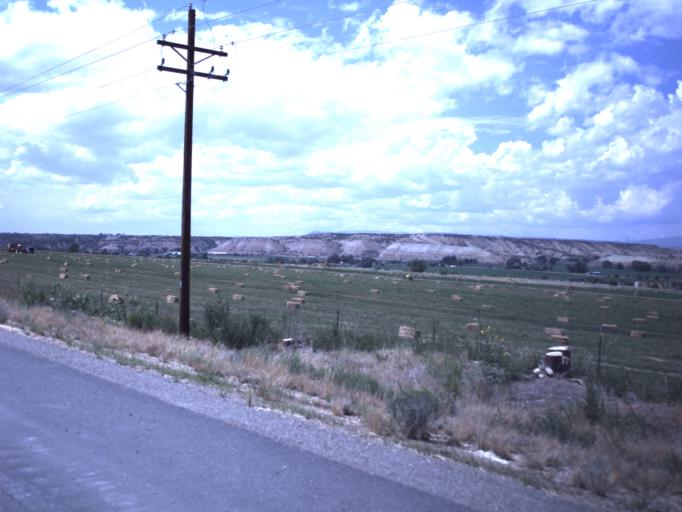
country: US
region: Utah
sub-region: Duchesne County
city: Duchesne
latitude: 40.1716
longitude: -110.3412
